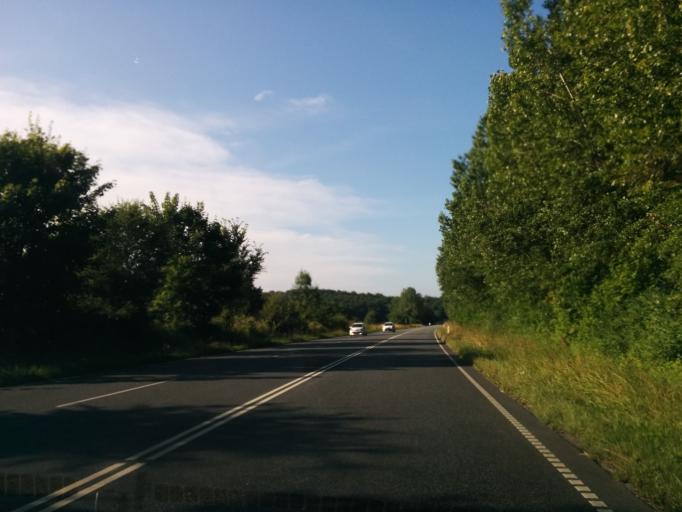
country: DK
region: Central Jutland
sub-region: Arhus Kommune
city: Beder
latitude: 56.0774
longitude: 10.2090
